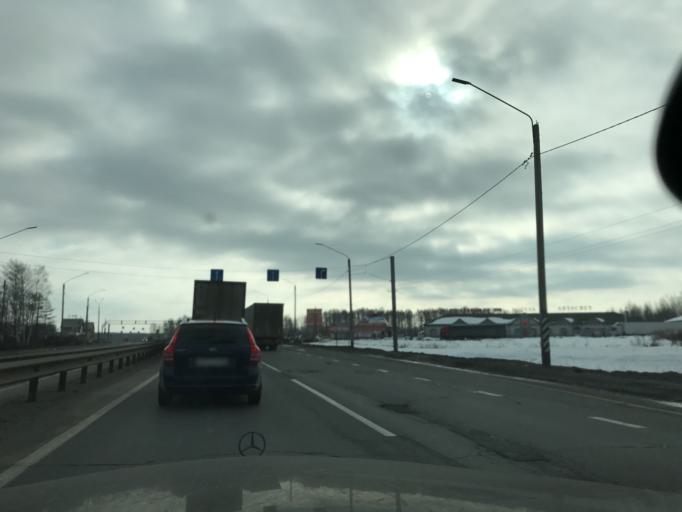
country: RU
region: Vladimir
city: Vyazniki
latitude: 56.2230
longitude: 42.1325
